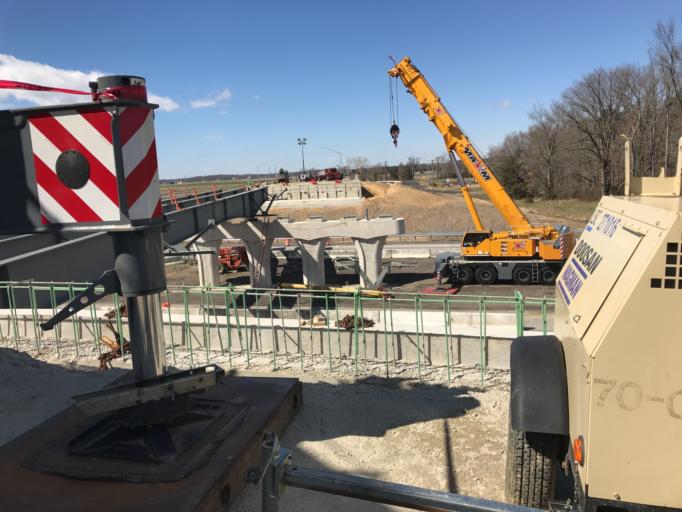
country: US
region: Maryland
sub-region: Queen Anne's County
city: Centreville
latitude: 39.0275
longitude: -76.0260
